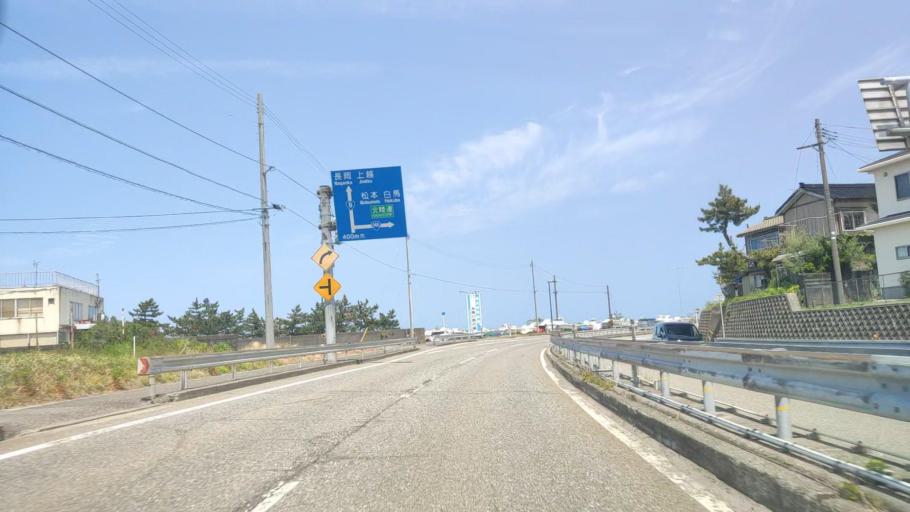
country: JP
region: Niigata
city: Itoigawa
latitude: 37.0427
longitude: 137.8463
